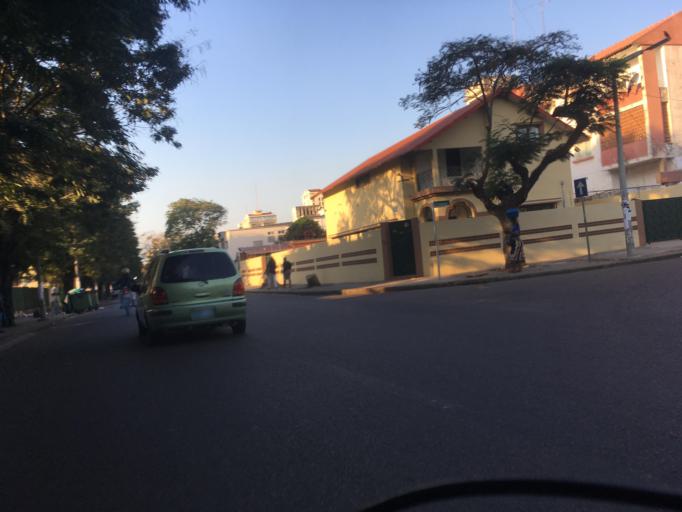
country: MZ
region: Maputo City
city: Maputo
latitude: -25.9703
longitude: 32.5904
